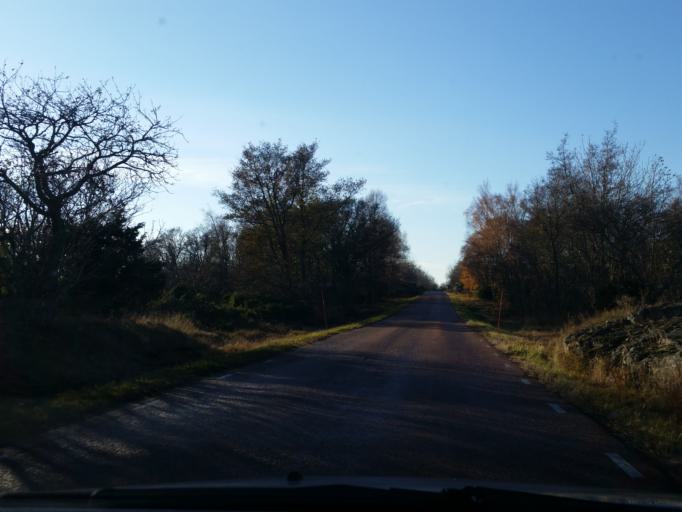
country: AX
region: Alands skaergard
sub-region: Braendoe
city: Braendoe
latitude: 60.4282
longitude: 21.0100
